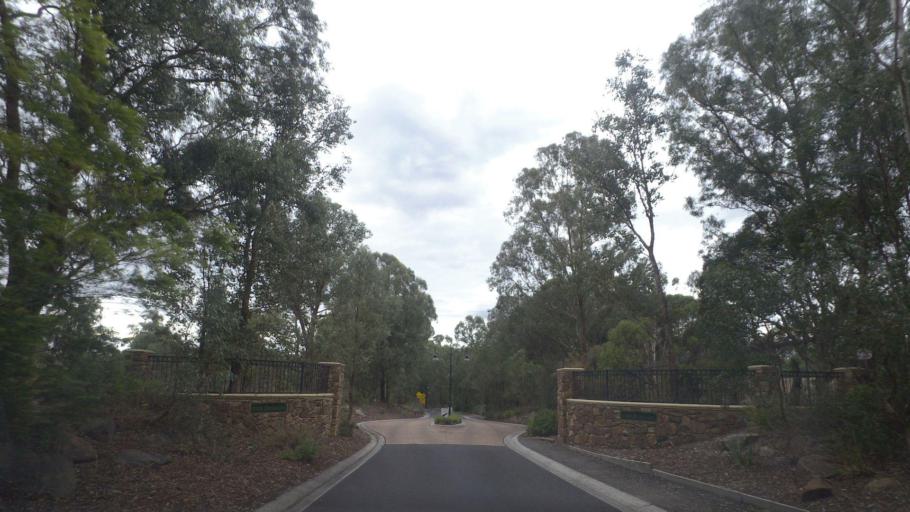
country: AU
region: Victoria
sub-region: Nillumbik
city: Eltham
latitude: -37.7471
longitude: 145.1696
